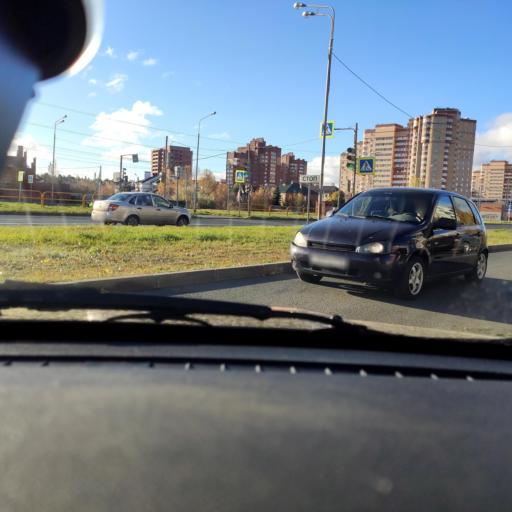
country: RU
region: Samara
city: Tol'yatti
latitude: 53.5417
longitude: 49.3645
